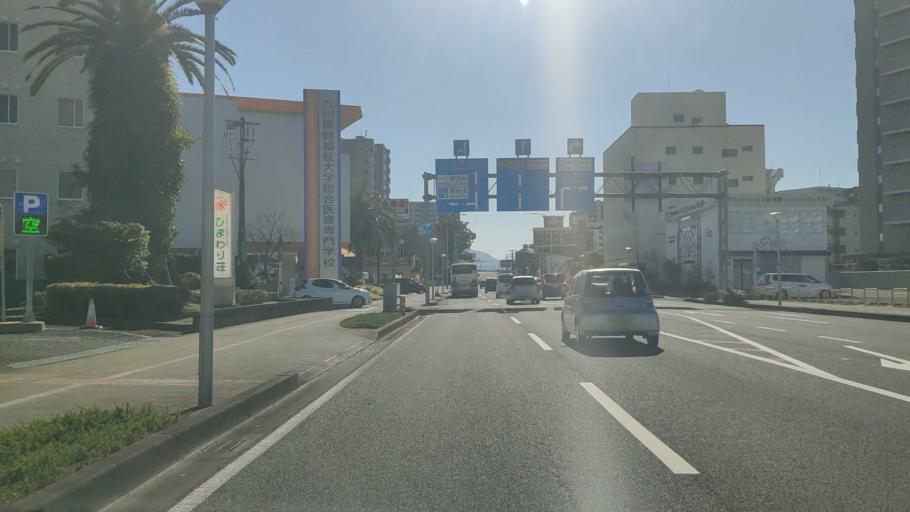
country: JP
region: Miyazaki
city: Miyazaki-shi
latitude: 31.9092
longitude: 131.4291
